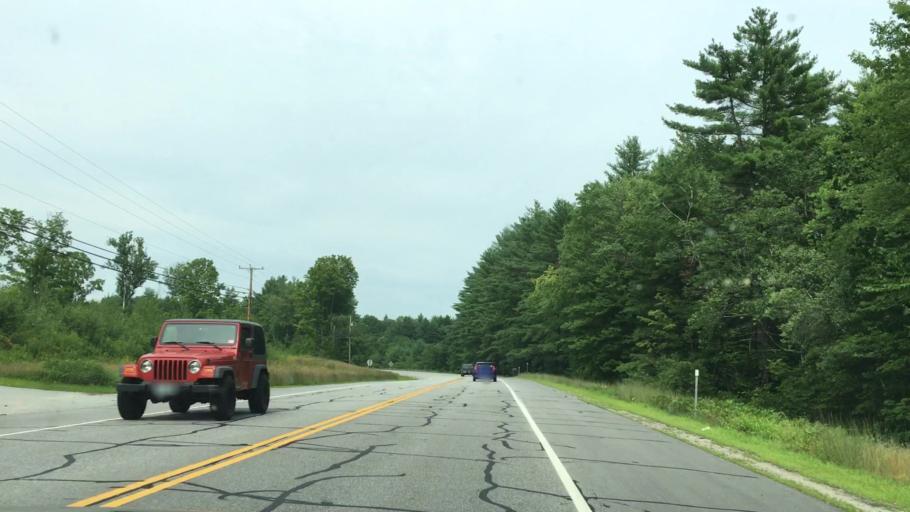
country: US
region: New Hampshire
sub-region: Hillsborough County
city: Antrim
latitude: 43.0482
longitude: -71.9284
